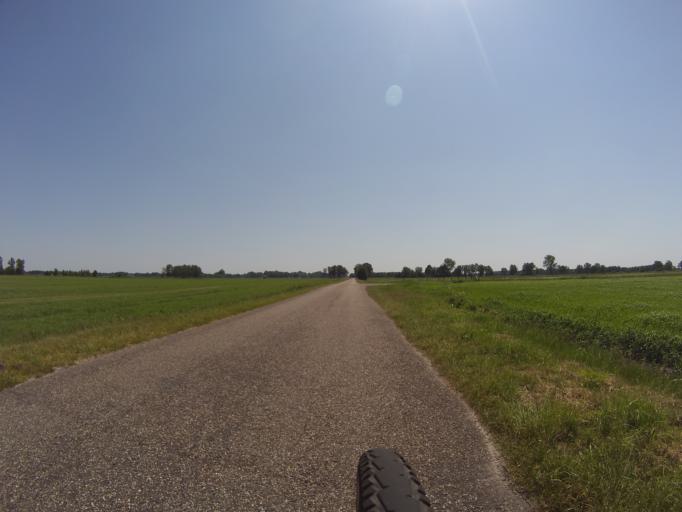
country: NL
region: Drenthe
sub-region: Gemeente Emmen
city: Schoonebeek
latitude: 52.6819
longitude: 6.8535
